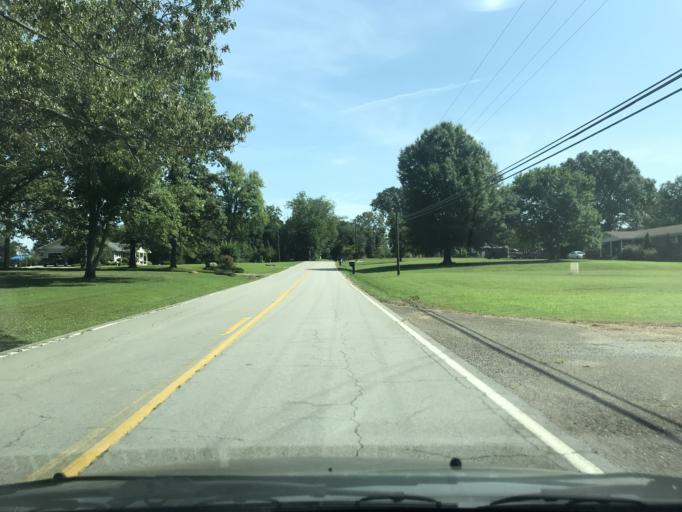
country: US
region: Tennessee
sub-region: Hamilton County
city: Lakesite
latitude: 35.2661
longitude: -85.0612
